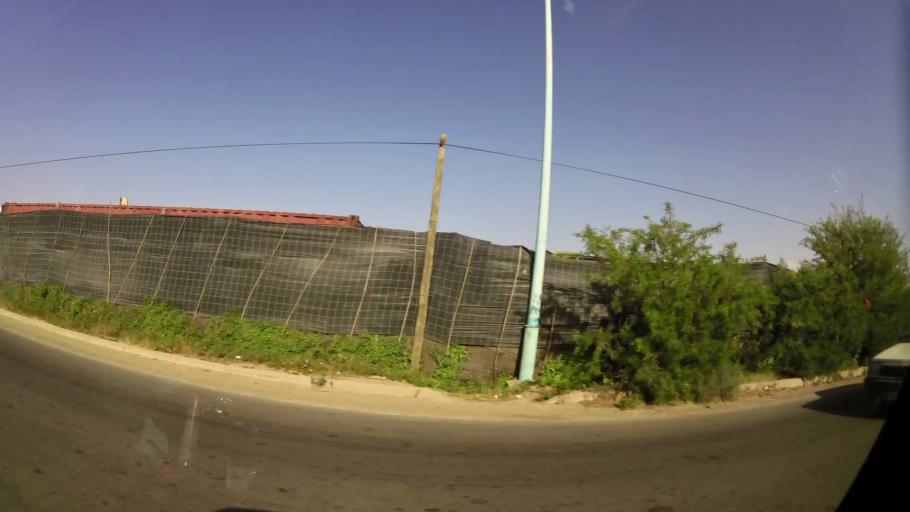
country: MA
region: Souss-Massa-Draa
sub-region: Inezgane-Ait Mellou
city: Inezgane
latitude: 30.3628
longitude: -9.5060
